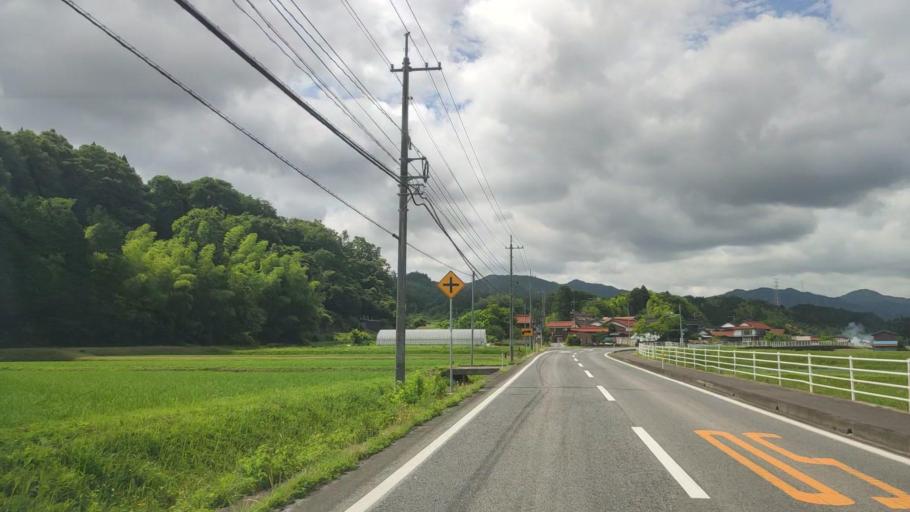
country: JP
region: Tottori
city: Yonago
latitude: 35.3054
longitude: 133.4174
